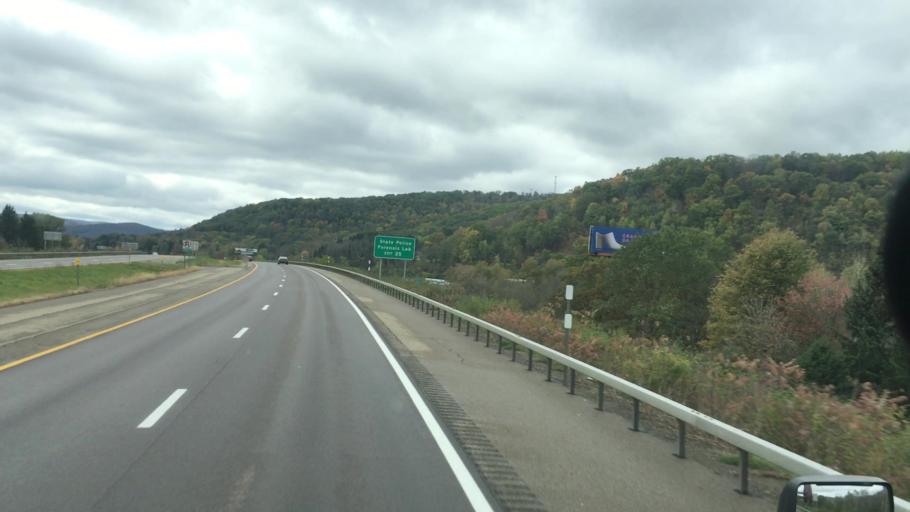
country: US
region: New York
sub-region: Cattaraugus County
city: Olean
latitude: 42.0995
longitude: -78.4360
